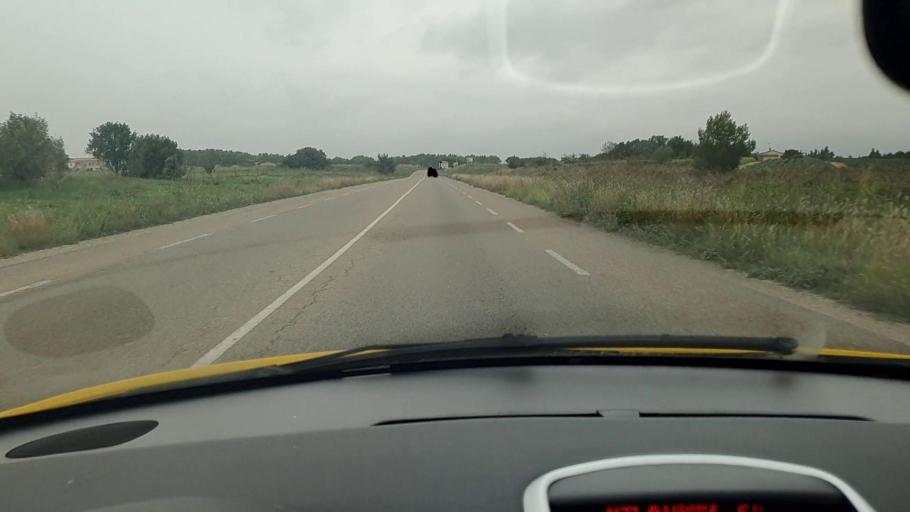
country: FR
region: Languedoc-Roussillon
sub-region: Departement du Gard
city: Le Cailar
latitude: 43.6888
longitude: 4.2398
